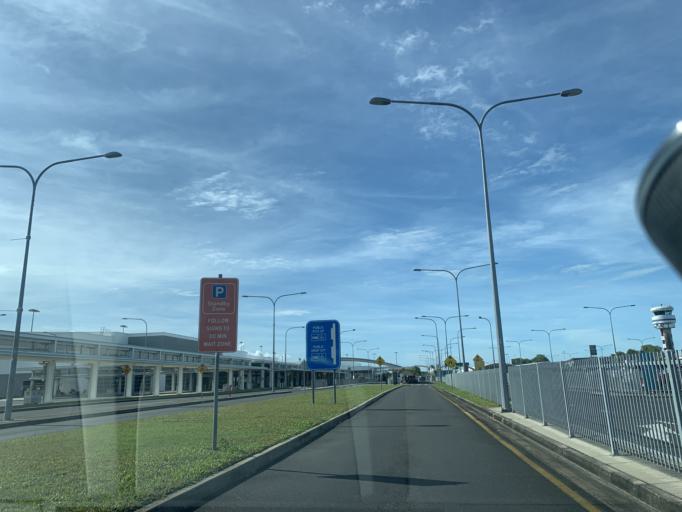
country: AU
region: Queensland
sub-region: Cairns
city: Cairns
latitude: -16.8787
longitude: 145.7552
